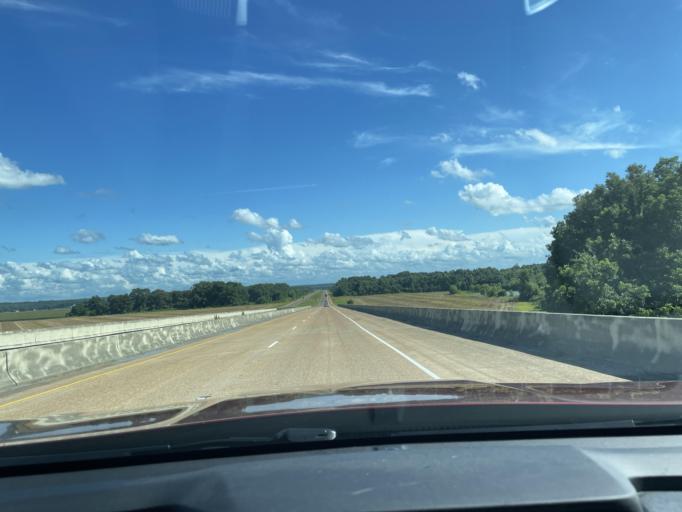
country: US
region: Mississippi
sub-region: Yazoo County
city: Yazoo City
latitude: 32.9248
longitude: -90.4126
